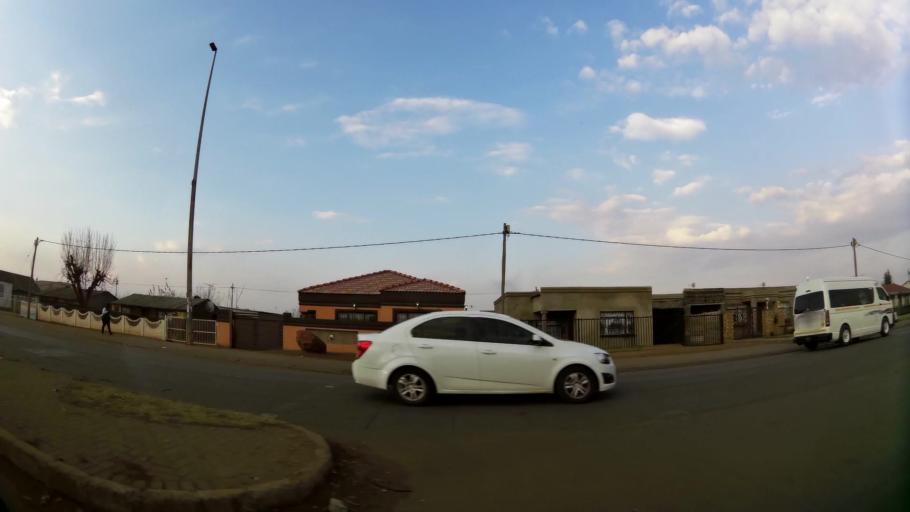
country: ZA
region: Gauteng
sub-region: City of Johannesburg Metropolitan Municipality
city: Orange Farm
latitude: -26.5666
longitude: 27.8353
